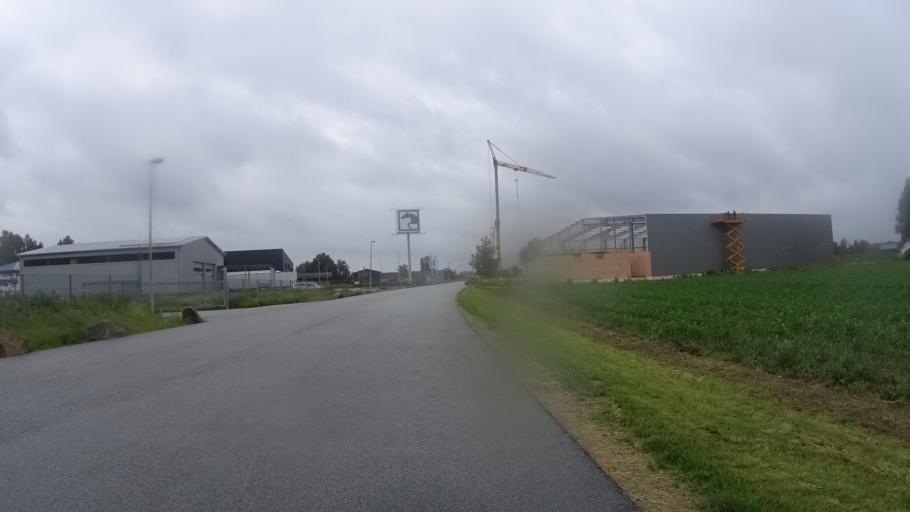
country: AT
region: Upper Austria
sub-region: Politischer Bezirk Scharding
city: Scharding
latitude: 48.4407
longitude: 13.3880
